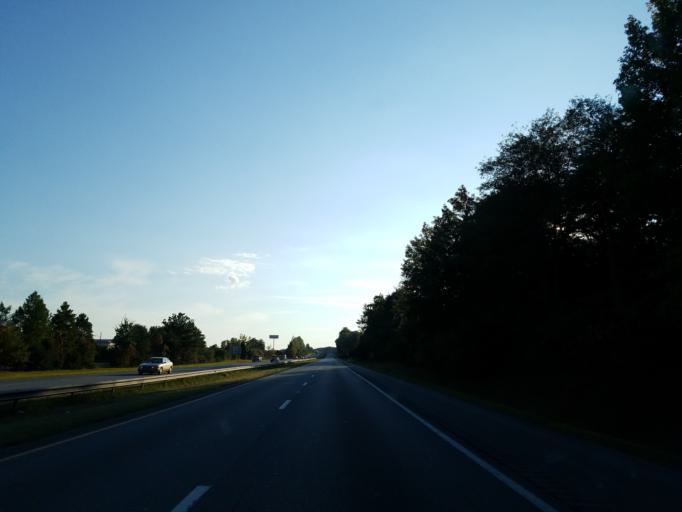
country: US
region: North Carolina
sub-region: Cleveland County
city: Kings Mountain
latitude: 35.2334
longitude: -81.3195
